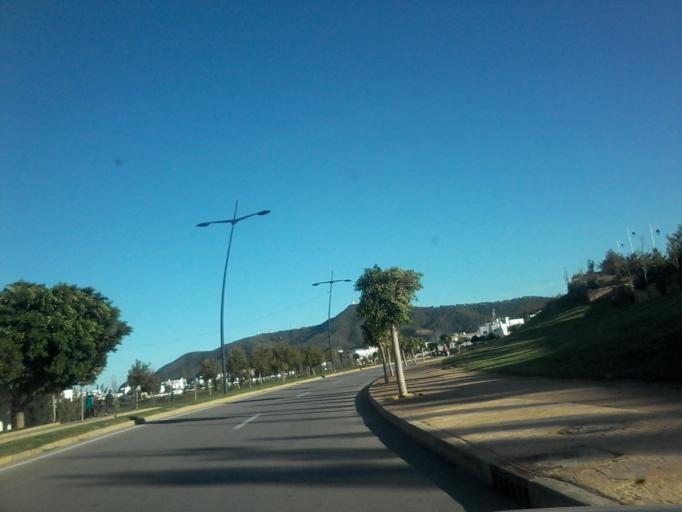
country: MA
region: Tanger-Tetouan
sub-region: Tetouan
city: Martil
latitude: 35.6953
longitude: -5.3350
